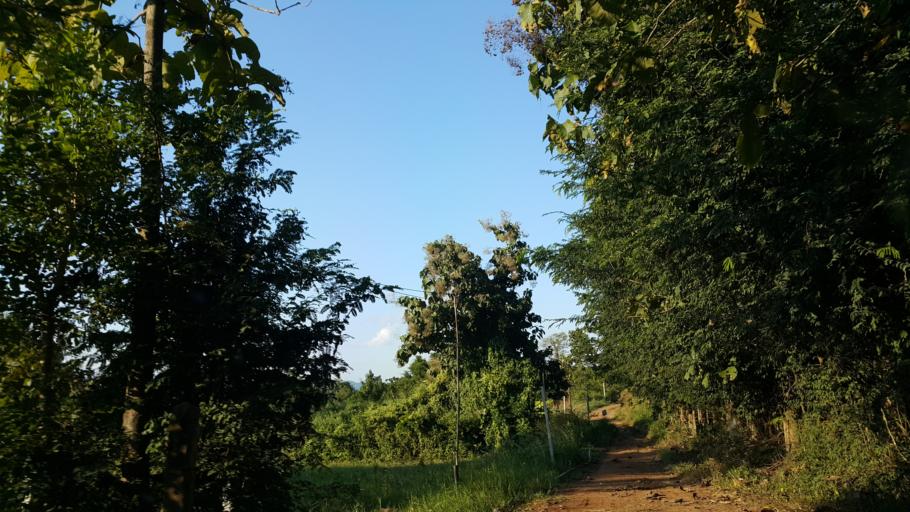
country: TH
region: Chiang Mai
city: Mae On
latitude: 18.7532
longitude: 99.2662
